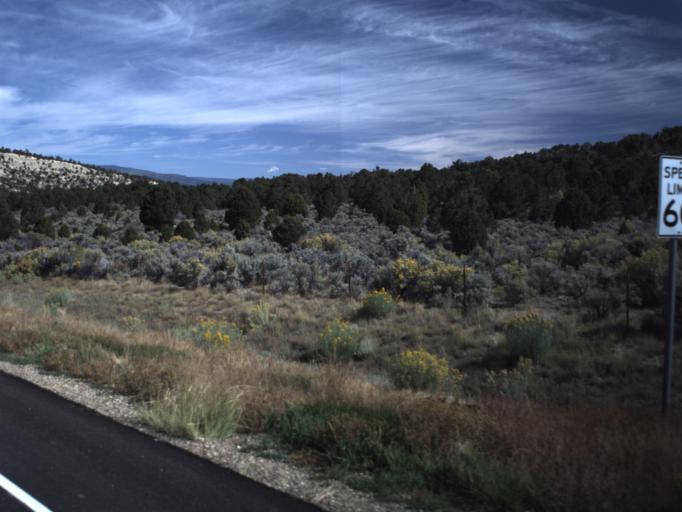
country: US
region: Utah
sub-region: Garfield County
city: Panguitch
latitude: 37.6427
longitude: -111.8448
